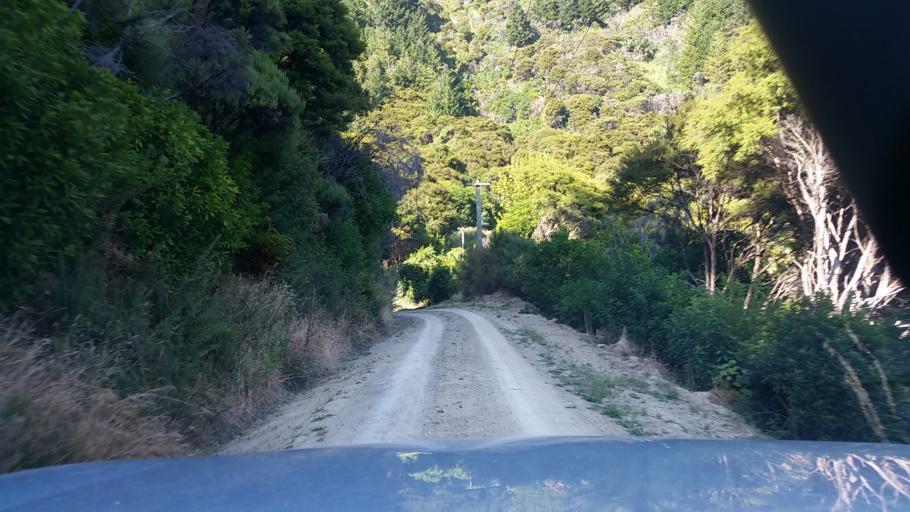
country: NZ
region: Marlborough
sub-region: Marlborough District
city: Picton
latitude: -41.3144
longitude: 174.1748
